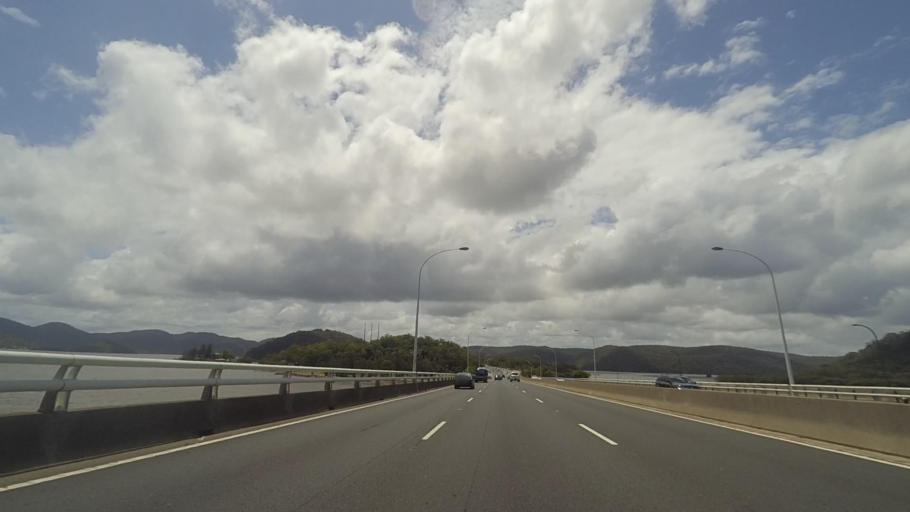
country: AU
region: New South Wales
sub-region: Hornsby Shire
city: Berowra
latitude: -33.5381
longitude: 151.1989
